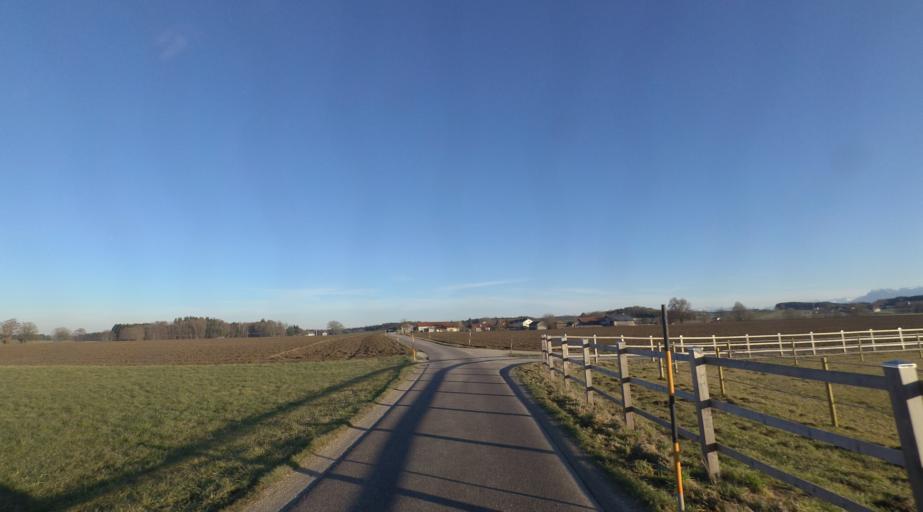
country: DE
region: Bavaria
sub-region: Upper Bavaria
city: Taching am See
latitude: 47.9931
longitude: 12.7494
